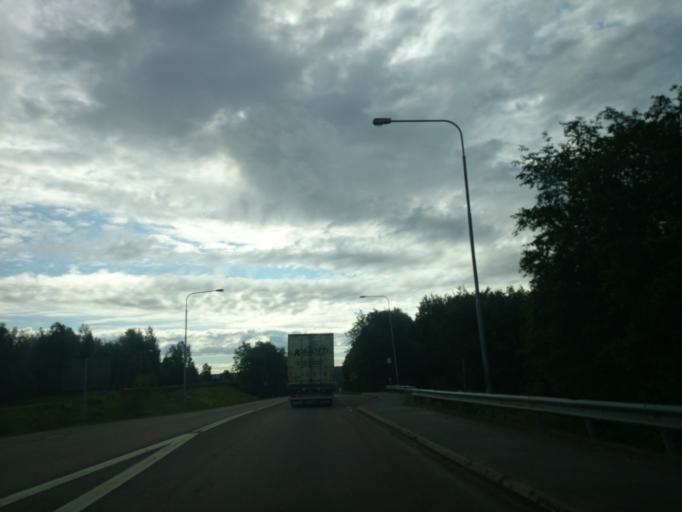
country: SE
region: Vaesternorrland
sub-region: Sundsvalls Kommun
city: Johannedal
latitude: 62.4126
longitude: 17.3693
